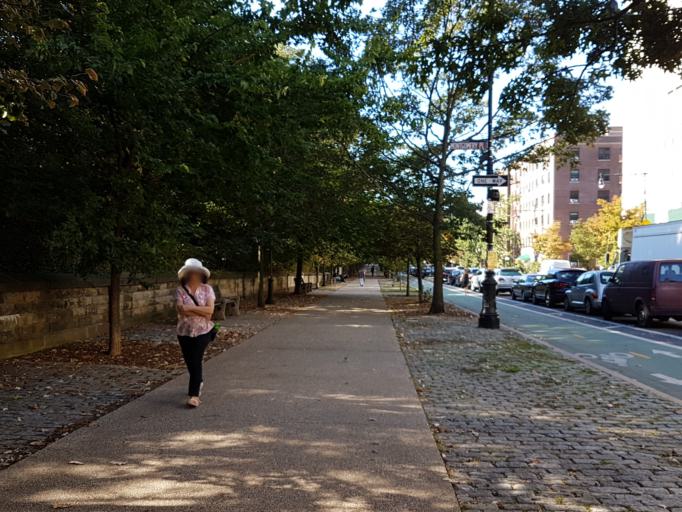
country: US
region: New York
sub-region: Kings County
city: Brooklyn
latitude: 40.6707
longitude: -73.9717
